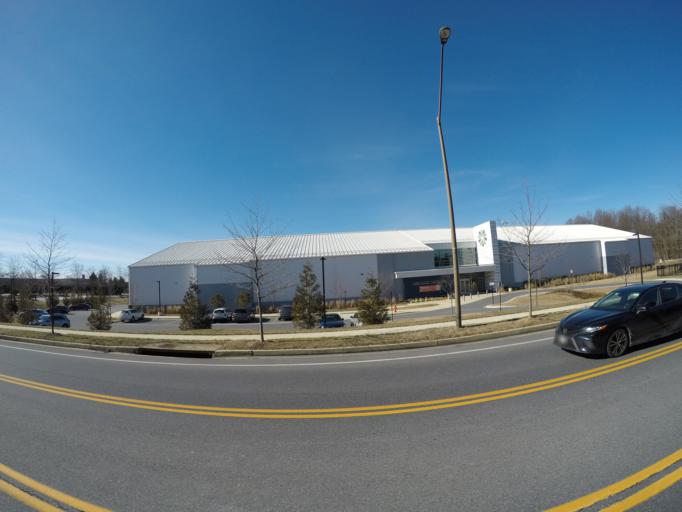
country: US
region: Maryland
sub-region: Howard County
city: Columbia
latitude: 39.2032
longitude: -76.8130
